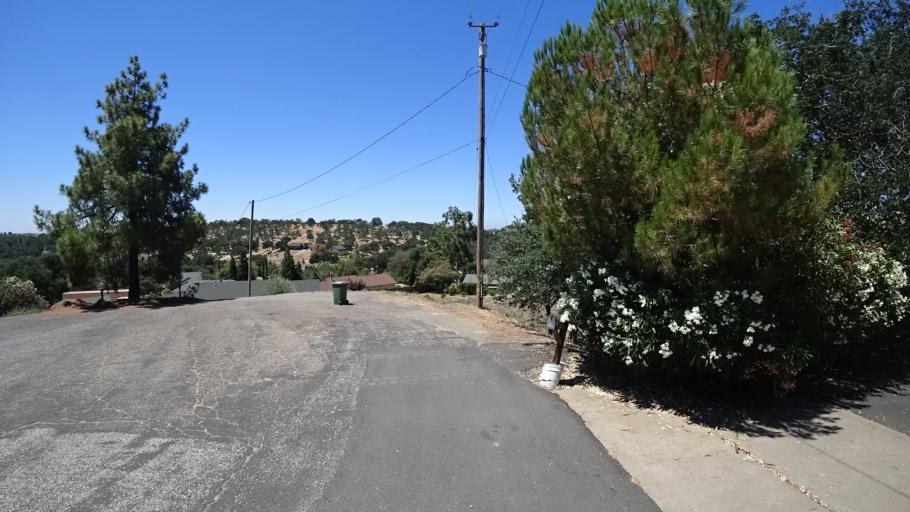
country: US
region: California
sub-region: Calaveras County
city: Rancho Calaveras
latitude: 38.1384
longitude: -120.8459
